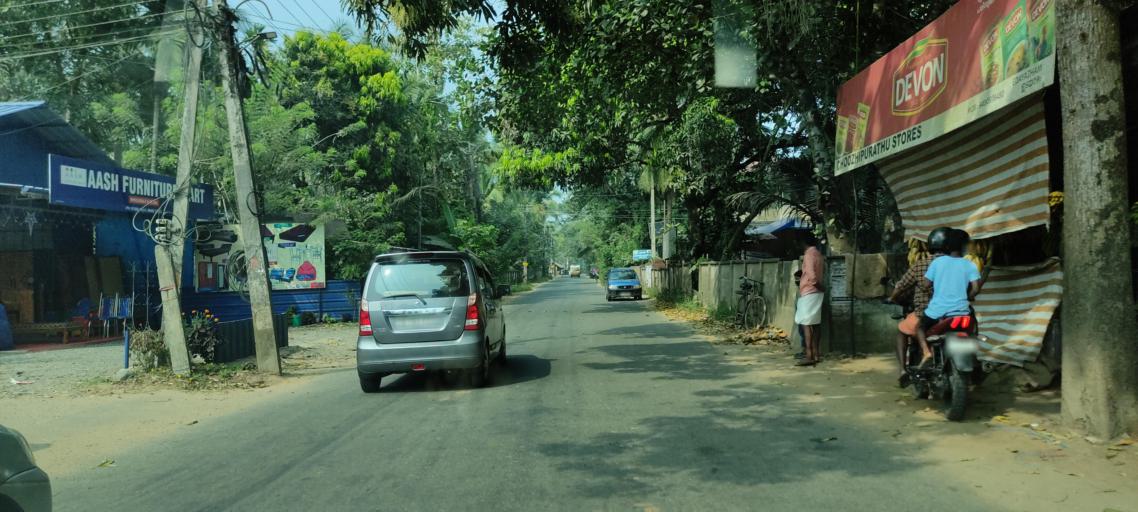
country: IN
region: Kerala
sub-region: Alappuzha
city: Shertallai
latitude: 9.6834
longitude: 76.4203
